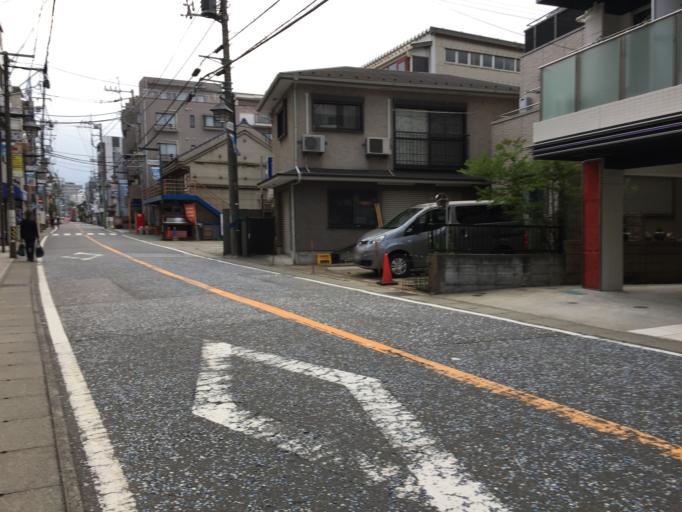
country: JP
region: Tokyo
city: Chofugaoka
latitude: 35.6057
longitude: 139.6182
